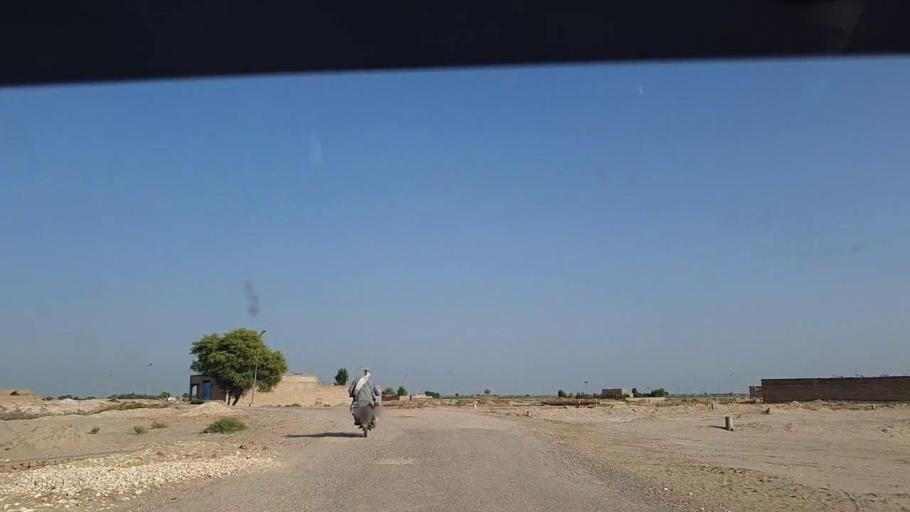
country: PK
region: Sindh
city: Tangwani
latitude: 28.2620
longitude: 69.0030
